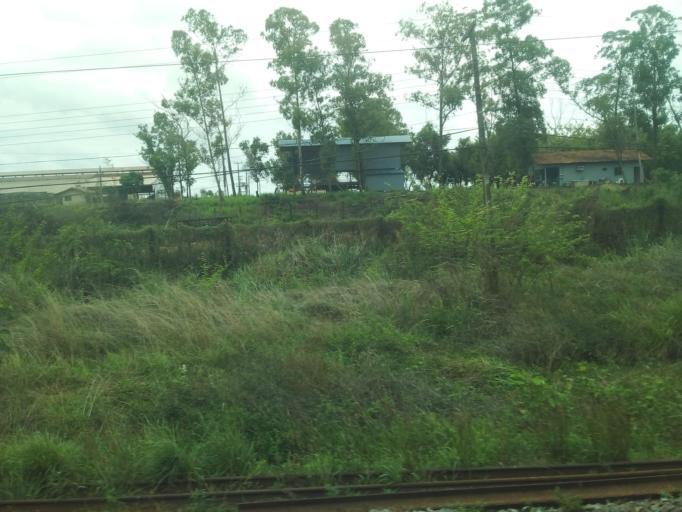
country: BR
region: Maranhao
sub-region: Santa Ines
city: Santa Ines
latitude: -3.6987
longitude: -45.4207
